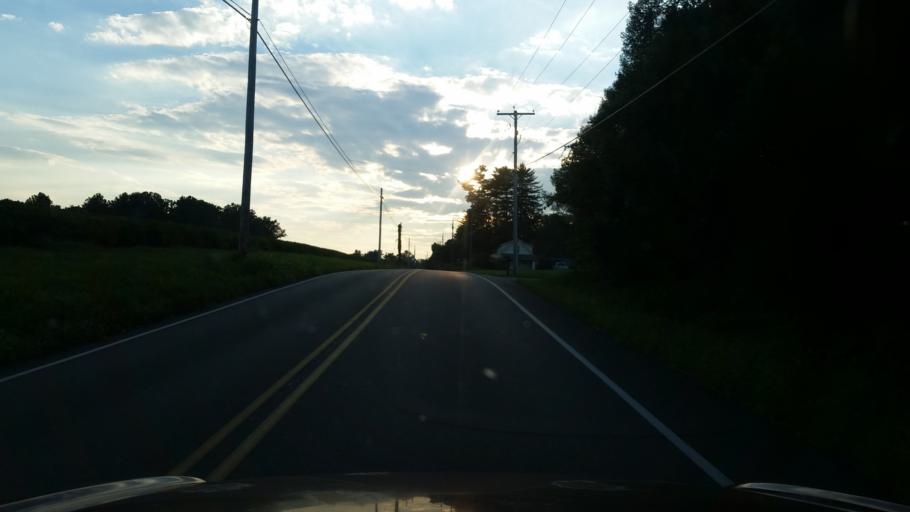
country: US
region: Pennsylvania
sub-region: Lebanon County
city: Campbelltown
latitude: 40.2454
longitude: -76.5289
